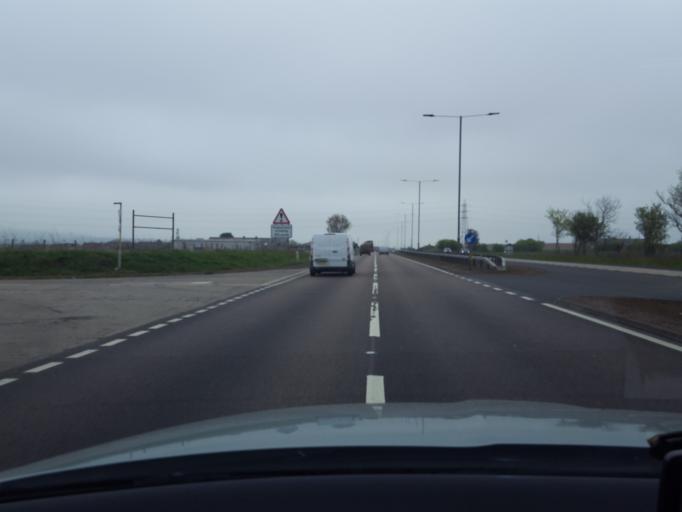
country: GB
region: Scotland
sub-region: Dundee City
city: Dundee
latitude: 56.5165
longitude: -2.9451
